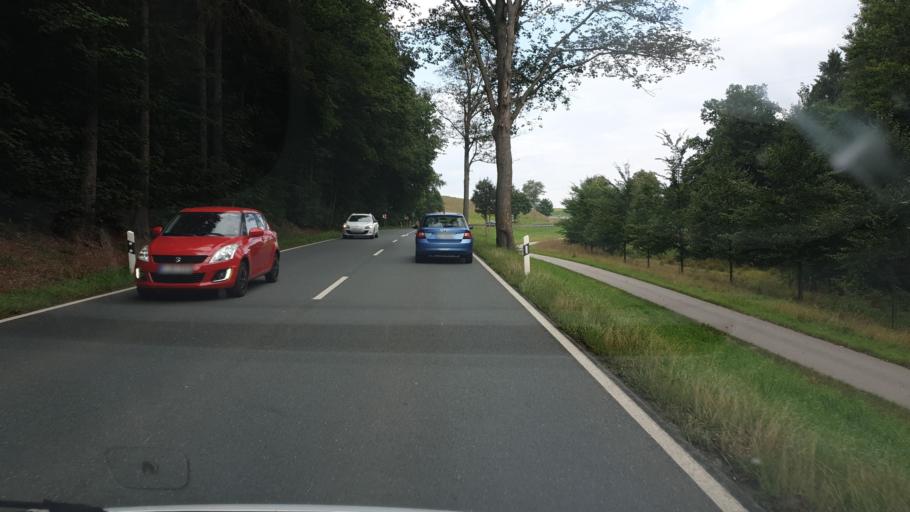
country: DE
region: Saxony
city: Lengenfeld
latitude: 50.5814
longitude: 12.3545
